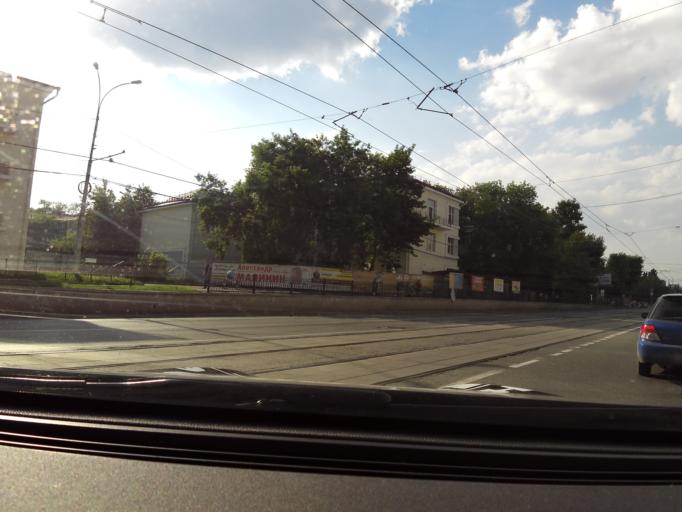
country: RU
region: Sverdlovsk
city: Yekaterinburg
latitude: 56.8344
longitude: 60.5827
